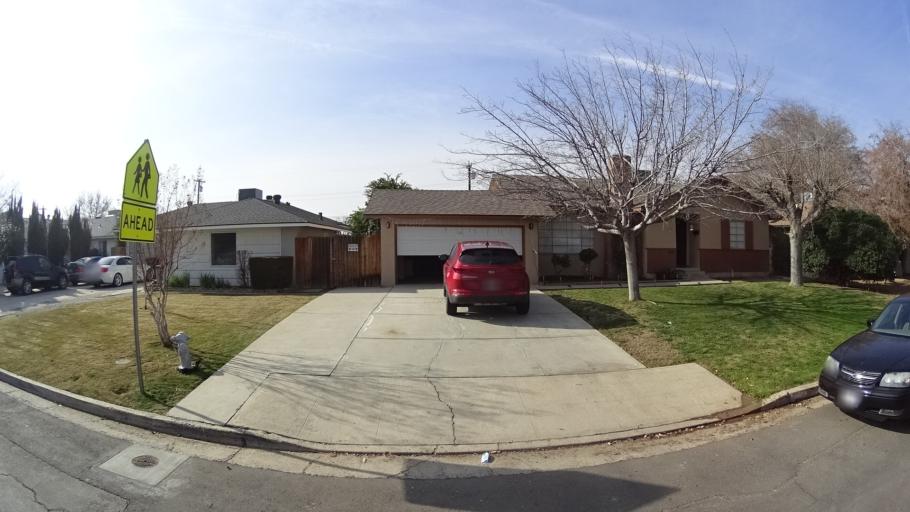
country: US
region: California
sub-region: Kern County
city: Oildale
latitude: 35.4009
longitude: -118.9808
